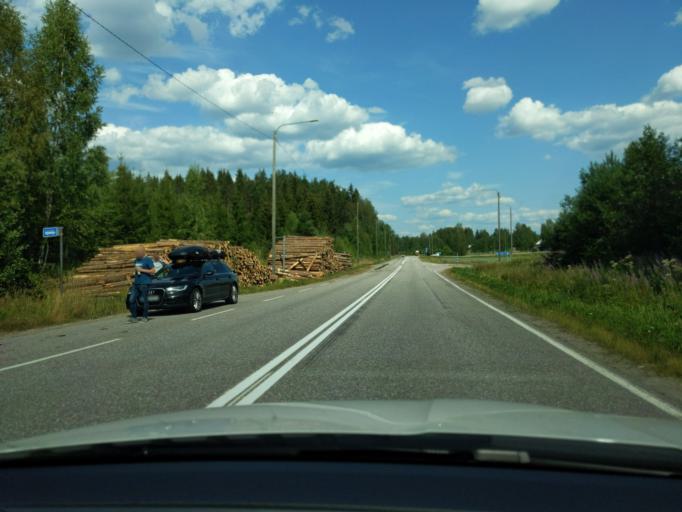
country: FI
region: Paijanne Tavastia
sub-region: Lahti
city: Heinola
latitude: 61.3321
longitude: 26.1619
